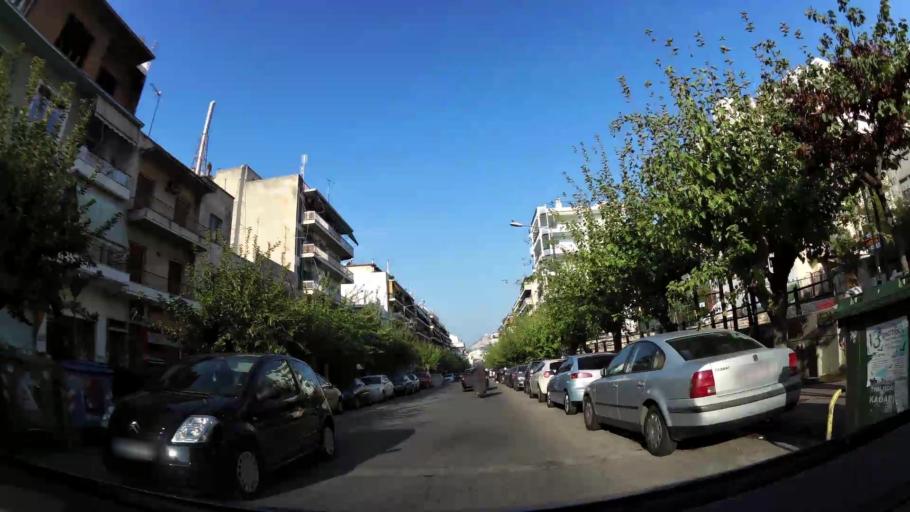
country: GR
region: Attica
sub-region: Nomarchia Athinas
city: Kaisariani
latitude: 37.9750
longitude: 23.7653
